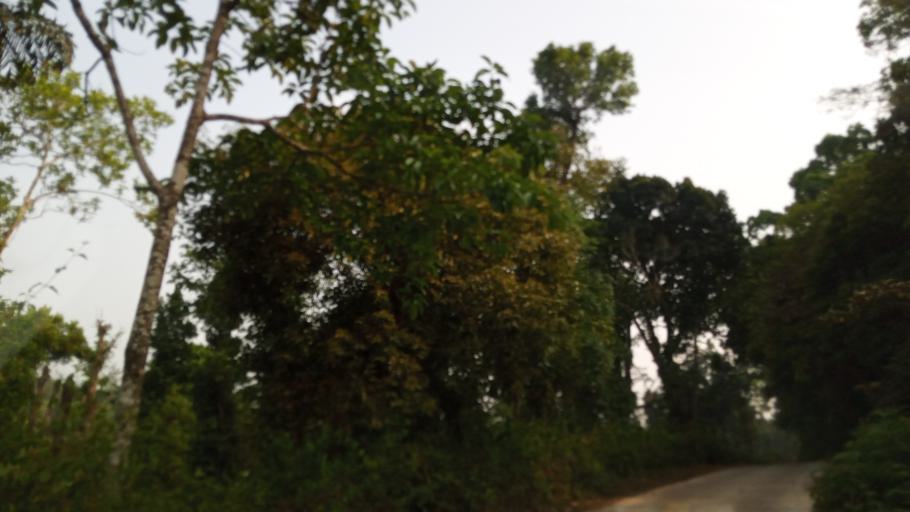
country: IN
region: Karnataka
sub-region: Chikmagalur
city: Mudigere
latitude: 13.0007
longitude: 75.6233
